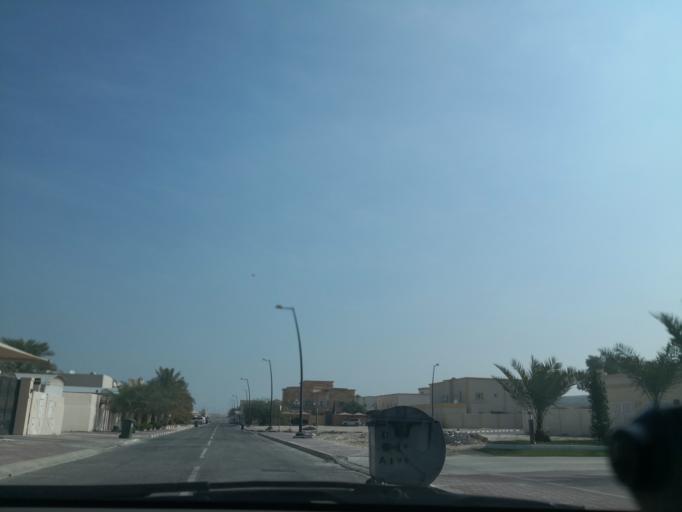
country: QA
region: Baladiyat ad Dawhah
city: Doha
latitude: 25.3459
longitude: 51.4894
